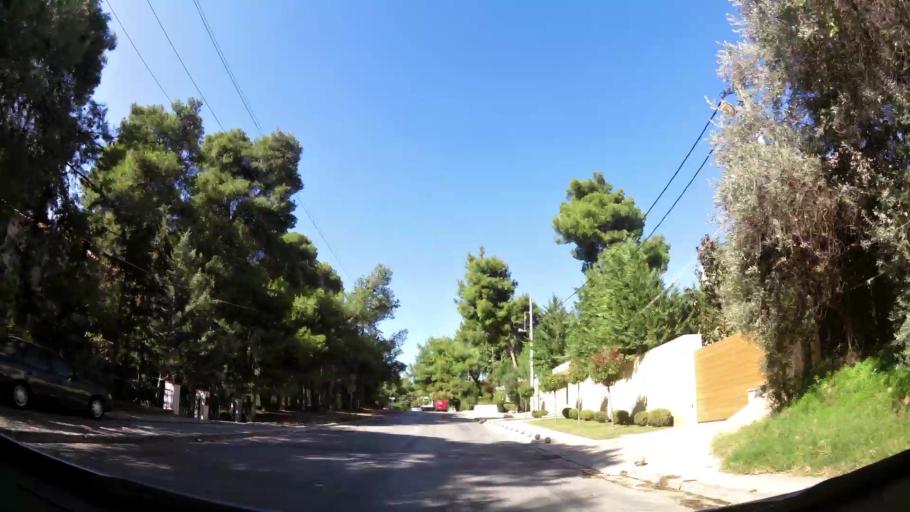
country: GR
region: Attica
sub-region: Nomarchia Athinas
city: Ekali
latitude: 38.1173
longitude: 23.8354
